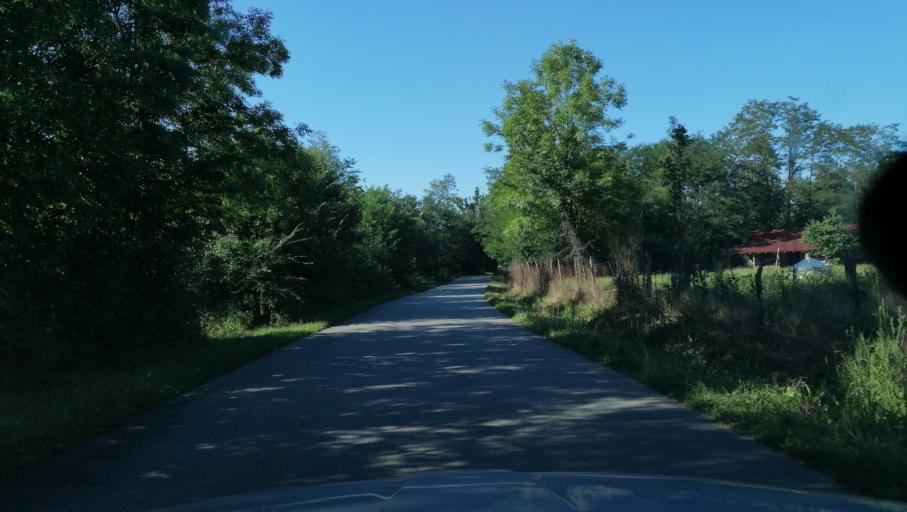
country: RS
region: Central Serbia
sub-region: Sumadijski Okrug
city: Knic
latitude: 43.8573
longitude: 20.6015
